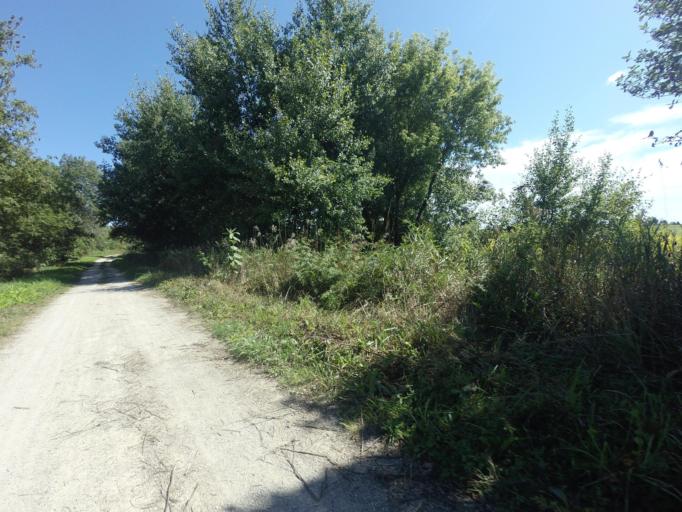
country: CA
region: Ontario
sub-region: Wellington County
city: Guelph
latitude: 43.7374
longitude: -80.3648
